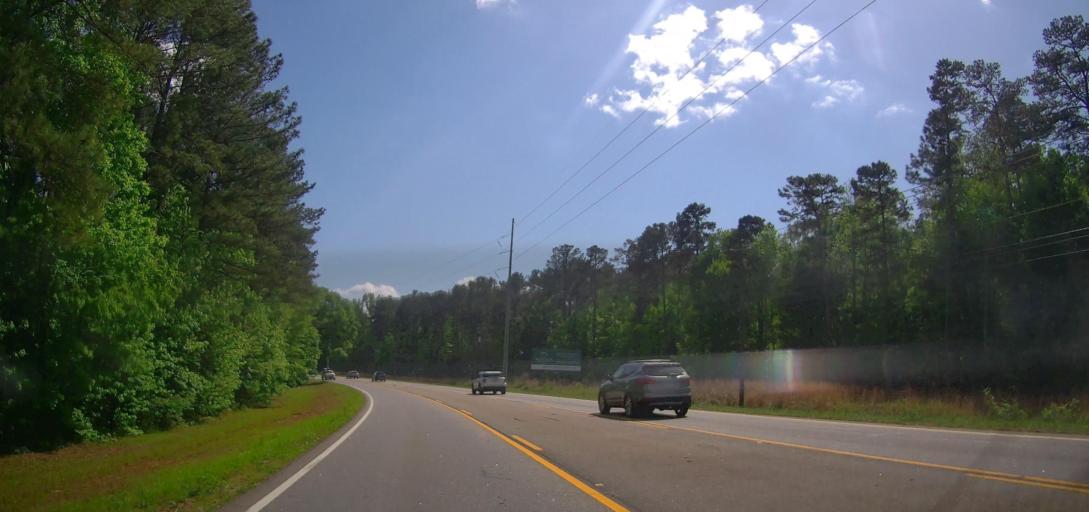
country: US
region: Georgia
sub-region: Putnam County
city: Jefferson
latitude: 33.4742
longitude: -83.2453
